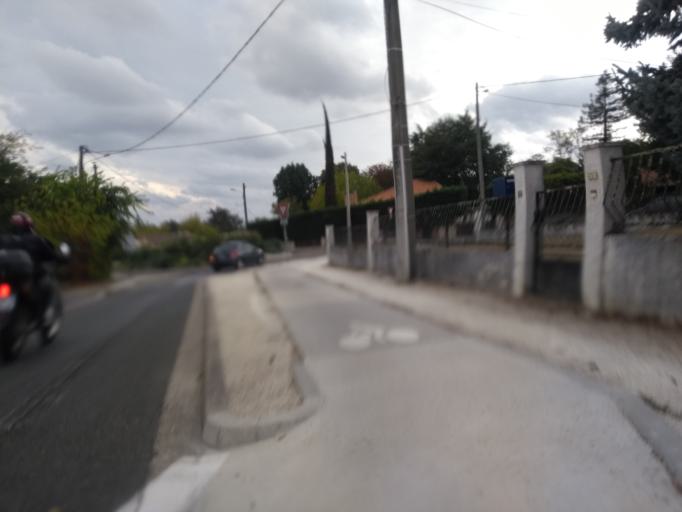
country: FR
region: Aquitaine
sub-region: Departement de la Gironde
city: Gradignan
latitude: 44.7799
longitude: -0.5946
